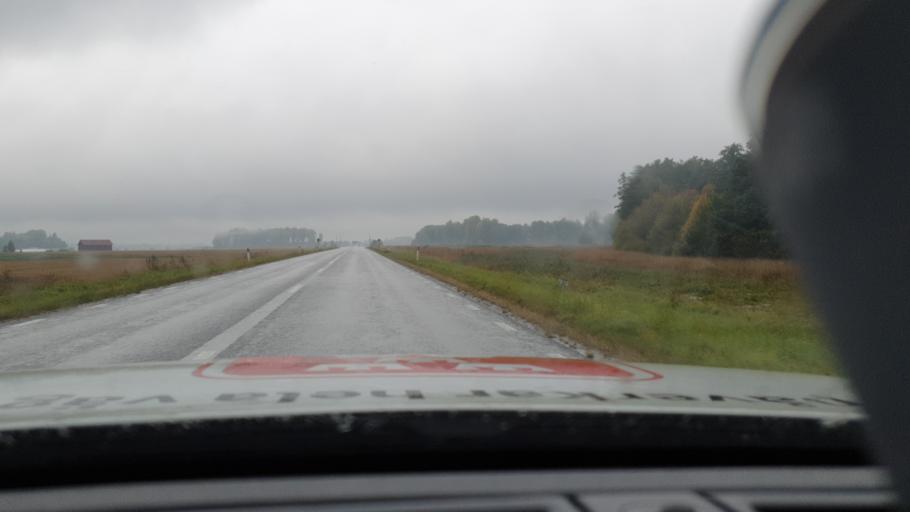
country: SE
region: Uppsala
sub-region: Tierps Kommun
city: Tierp
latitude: 60.3342
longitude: 17.5081
